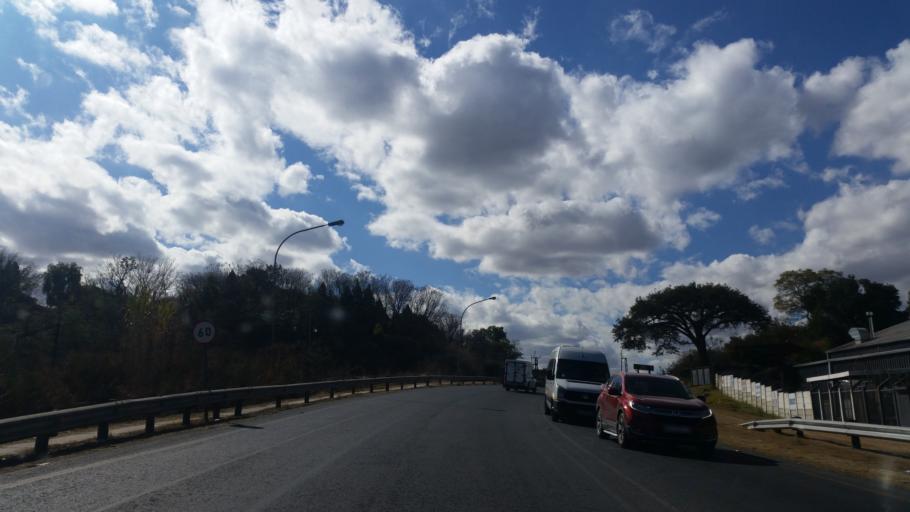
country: ZA
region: KwaZulu-Natal
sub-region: uThukela District Municipality
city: Ladysmith
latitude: -28.5503
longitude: 29.7907
